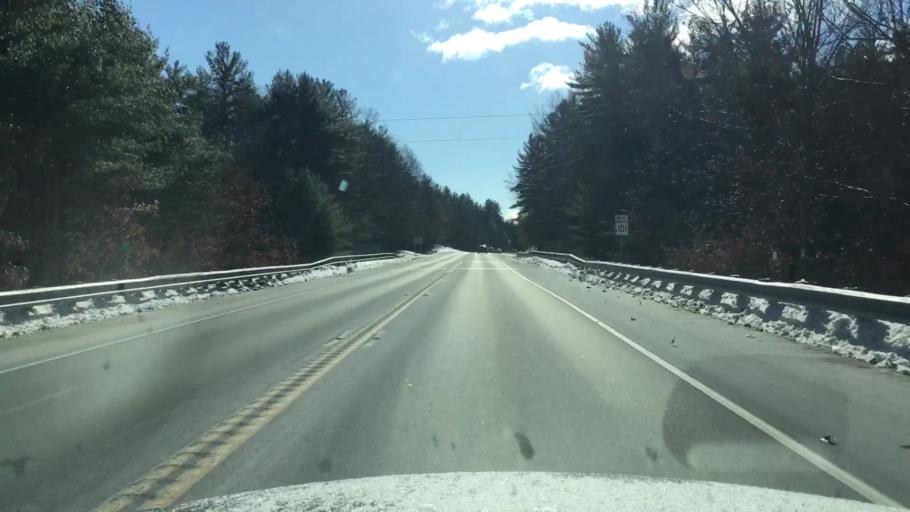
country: US
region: New Hampshire
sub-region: Hillsborough County
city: Milford
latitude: 42.8586
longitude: -71.6117
